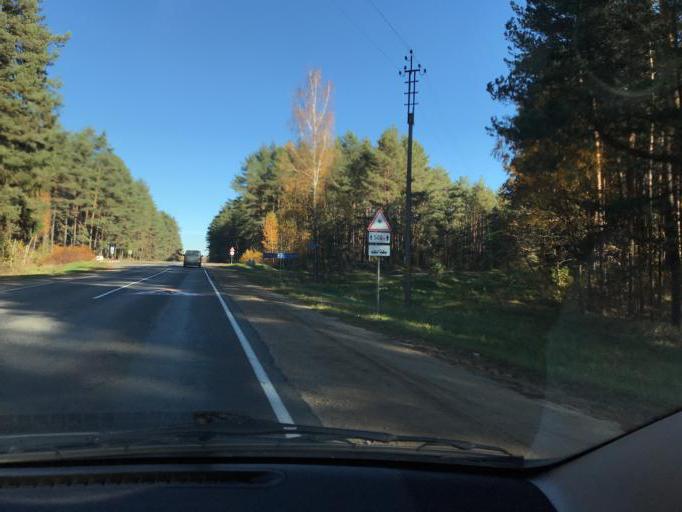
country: BY
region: Vitebsk
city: Polatsk
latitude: 55.3183
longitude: 28.7783
